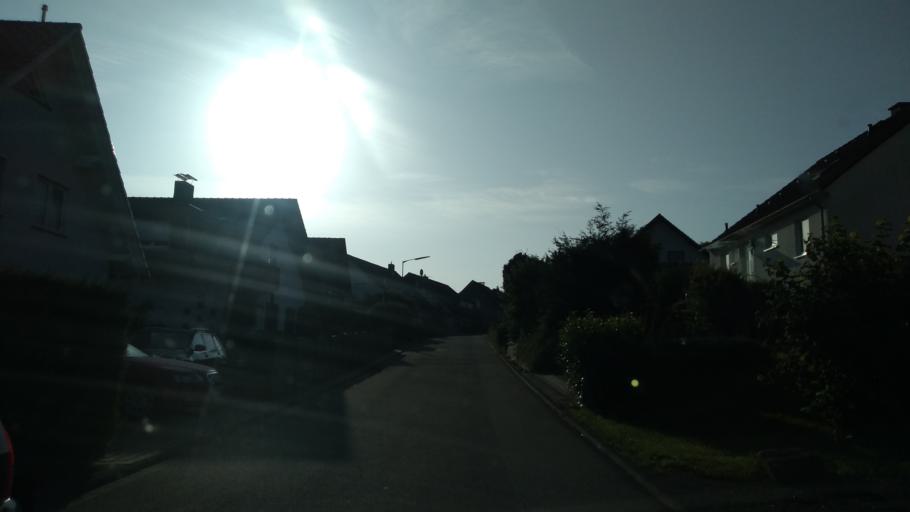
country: DE
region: North Rhine-Westphalia
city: Wiehl
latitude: 50.9595
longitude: 7.4949
